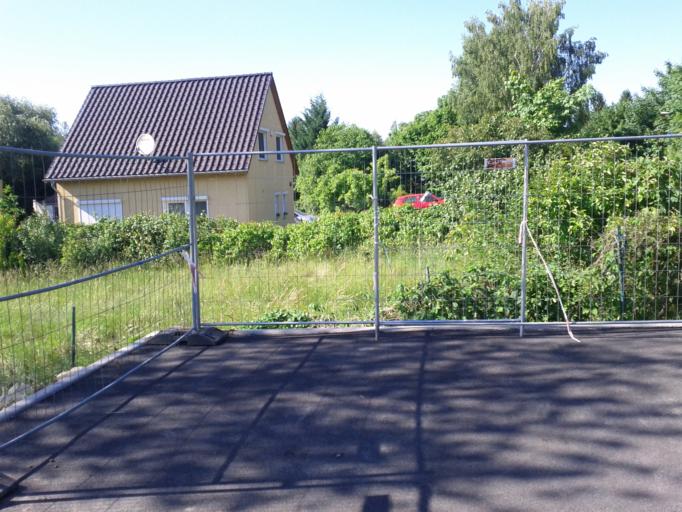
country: DE
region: Berlin
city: Mahlsdorf
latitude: 52.5079
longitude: 13.6150
